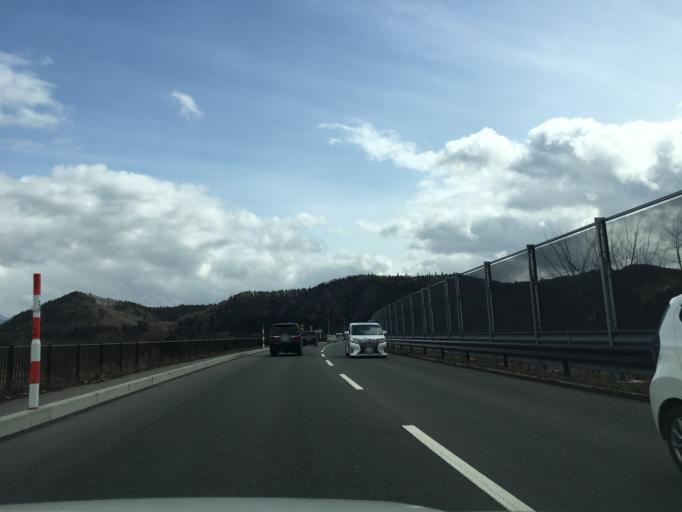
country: JP
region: Akita
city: Hanawa
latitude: 40.2270
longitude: 140.7139
